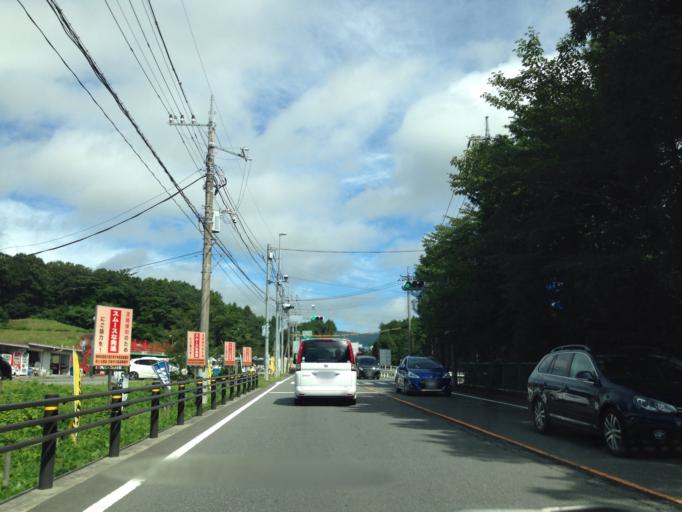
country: JP
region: Shizuoka
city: Gotemba
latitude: 35.3474
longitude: 138.8790
